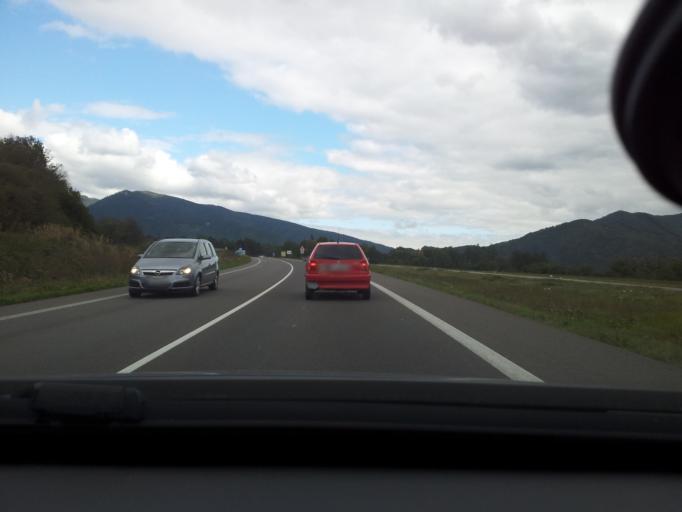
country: SK
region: Zilinsky
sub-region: Okres Zilina
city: Terchova
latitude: 49.1260
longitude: 19.0575
